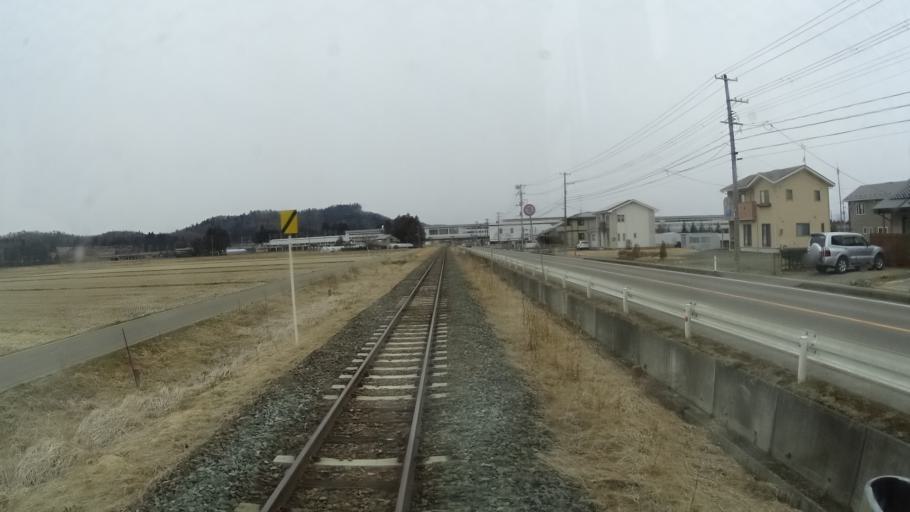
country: JP
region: Iwate
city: Hanamaki
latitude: 39.4066
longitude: 141.1786
